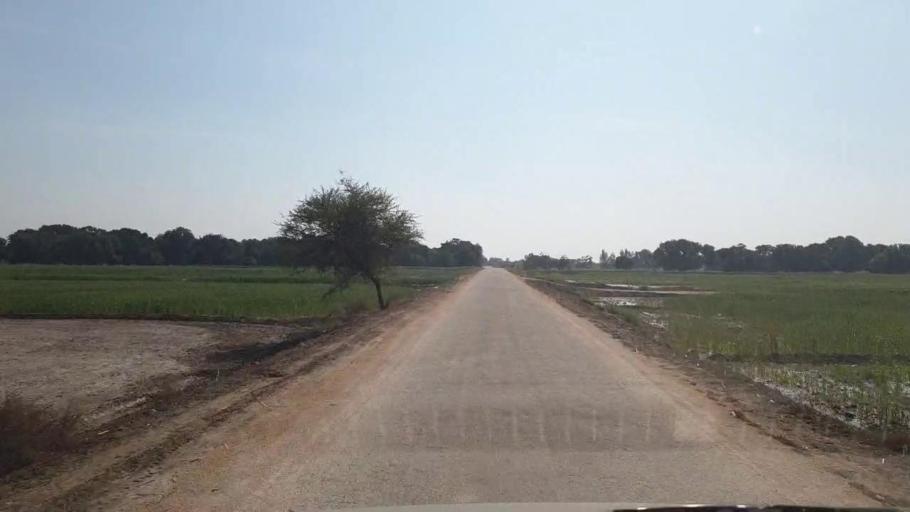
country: PK
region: Sindh
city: Chambar
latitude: 25.3808
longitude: 68.8052
